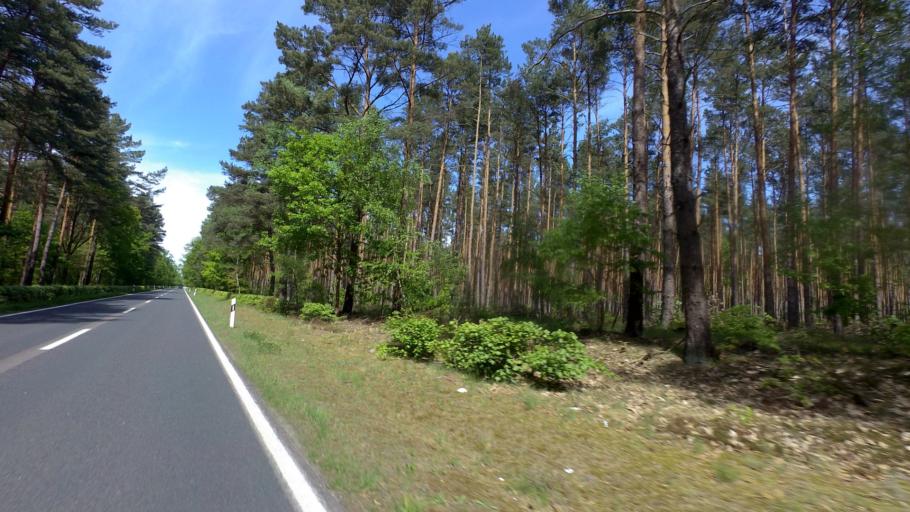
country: DE
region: Brandenburg
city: Sperenberg
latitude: 52.1178
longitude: 13.3694
